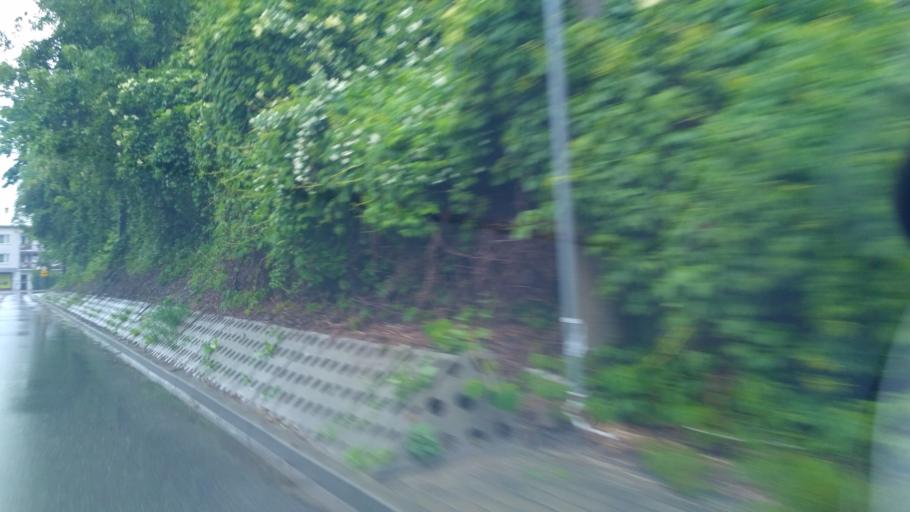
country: PL
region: Subcarpathian Voivodeship
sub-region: Powiat jasielski
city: Jaslo
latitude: 49.7480
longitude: 21.4706
